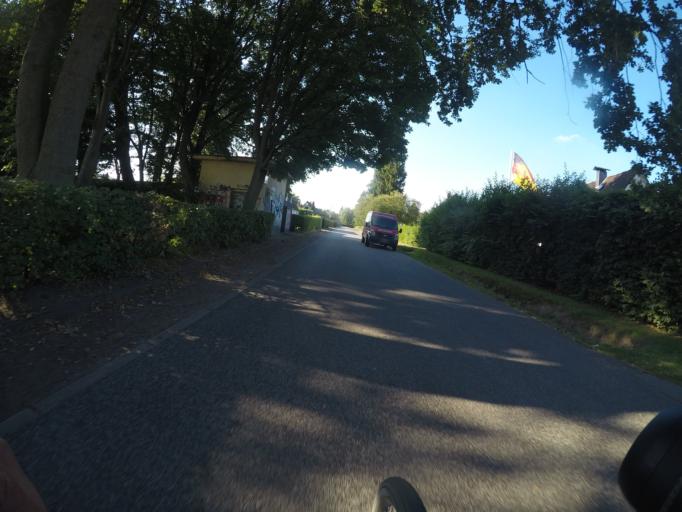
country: DE
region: Hamburg
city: Wandsbek
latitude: 53.5637
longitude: 10.1169
